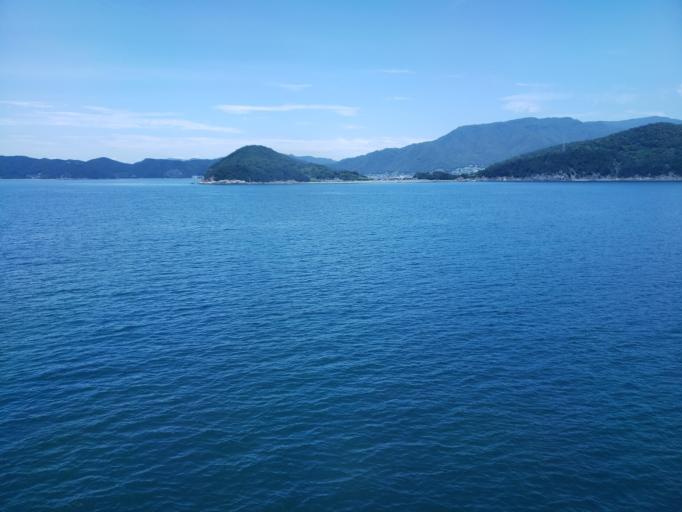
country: JP
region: Kagawa
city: Tonosho
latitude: 34.4359
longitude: 134.2926
